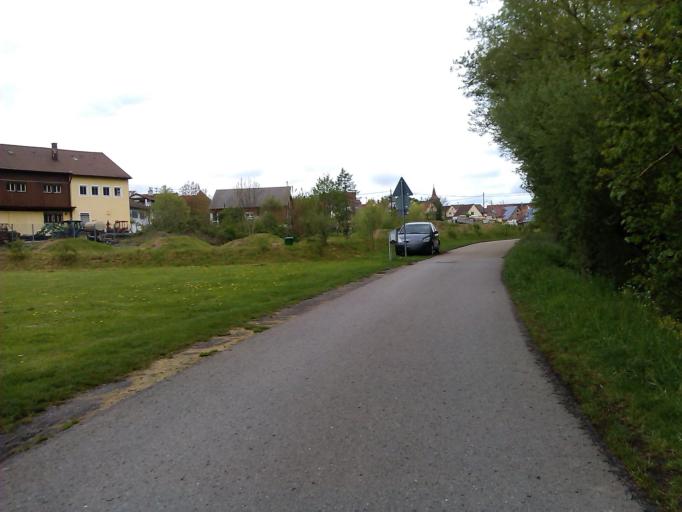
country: DE
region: Baden-Wuerttemberg
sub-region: Regierungsbezirk Stuttgart
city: Zaberfeld
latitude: 49.0557
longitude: 8.9328
